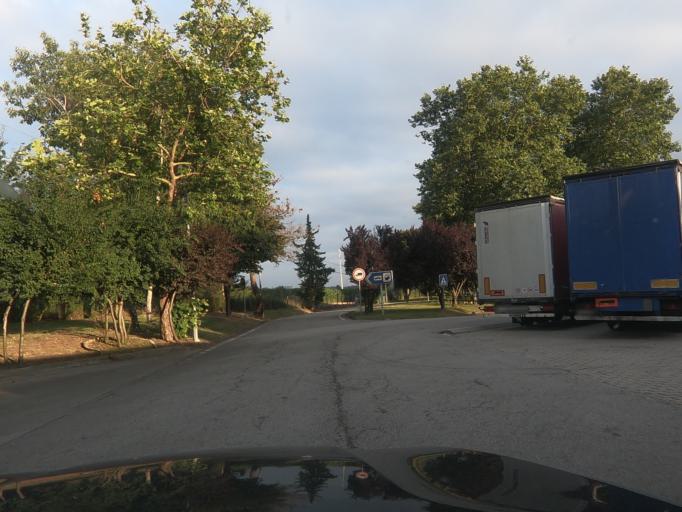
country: PT
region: Aveiro
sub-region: Estarreja
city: Salreu
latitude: 40.7557
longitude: -8.5346
